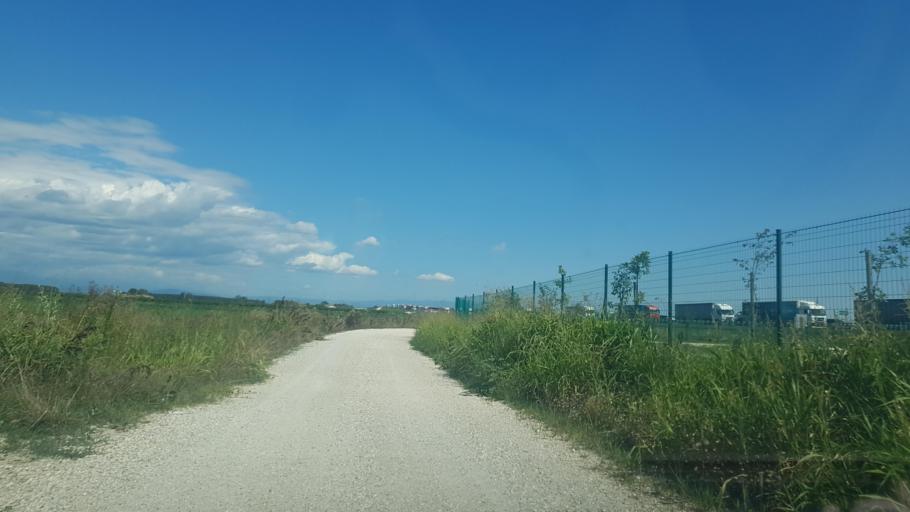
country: IT
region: Friuli Venezia Giulia
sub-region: Provincia di Udine
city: Muzzana del Turgnano
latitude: 45.8429
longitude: 13.1396
